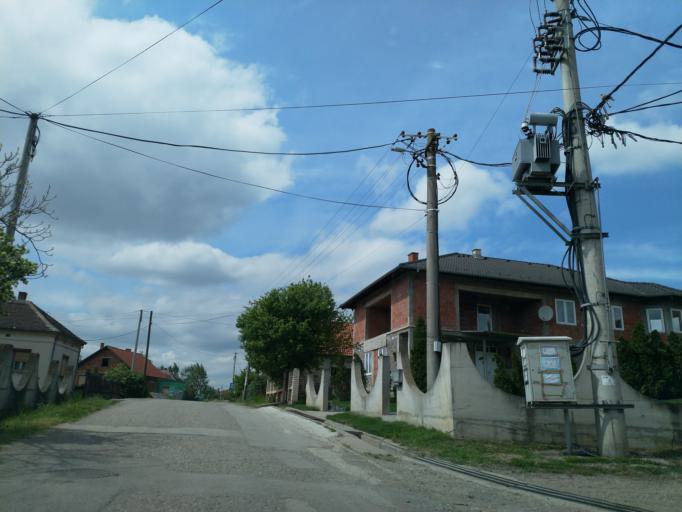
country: RS
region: Central Serbia
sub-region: Pomoravski Okrug
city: Paracin
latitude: 43.9383
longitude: 21.4916
